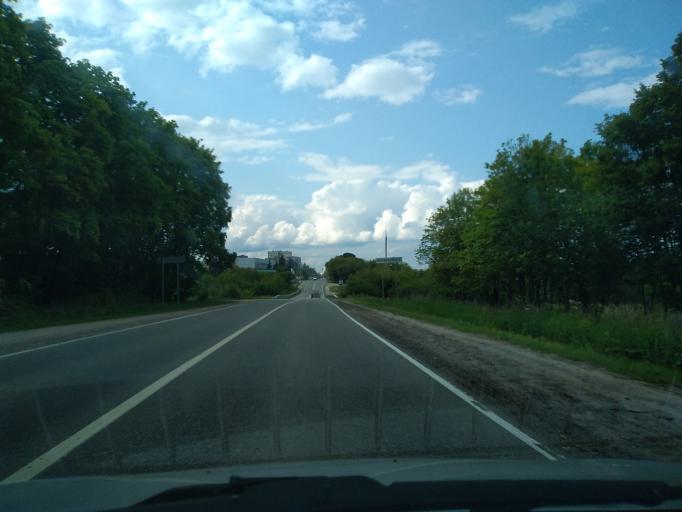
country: RU
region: Moskovskaya
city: Voskresensk
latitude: 55.3010
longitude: 38.6623
